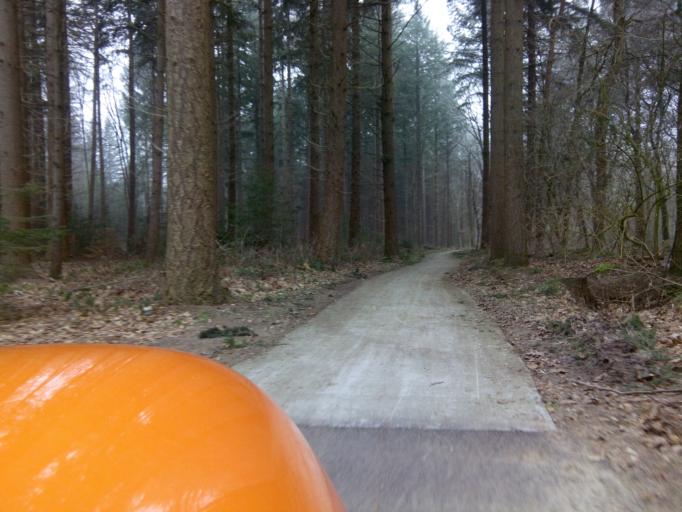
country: NL
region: Gelderland
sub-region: Gemeente Putten
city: Putten
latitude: 52.2435
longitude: 5.6465
